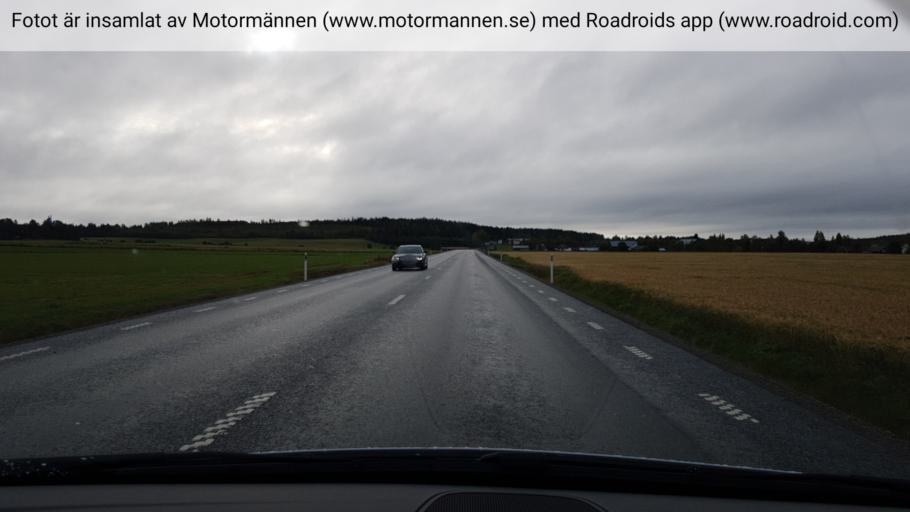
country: SE
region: Vaesterbotten
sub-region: Umea Kommun
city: Roback
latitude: 63.8708
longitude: 20.0726
